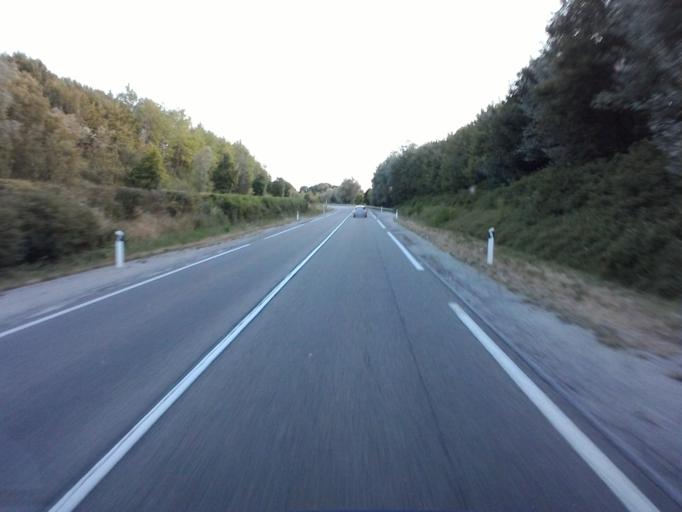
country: FR
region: Franche-Comte
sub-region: Departement du Doubs
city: Quingey
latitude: 47.0900
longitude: 5.8879
